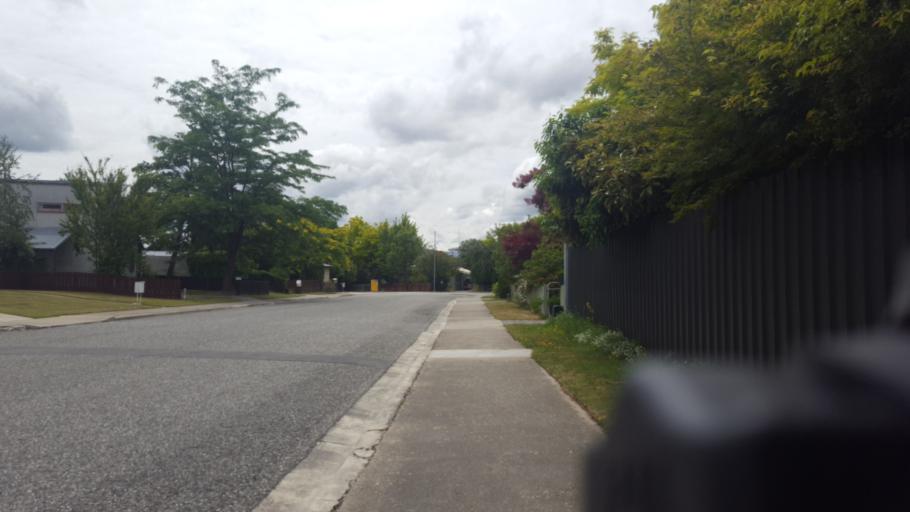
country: NZ
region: Otago
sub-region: Queenstown-Lakes District
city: Wanaka
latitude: -45.2492
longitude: 169.3775
